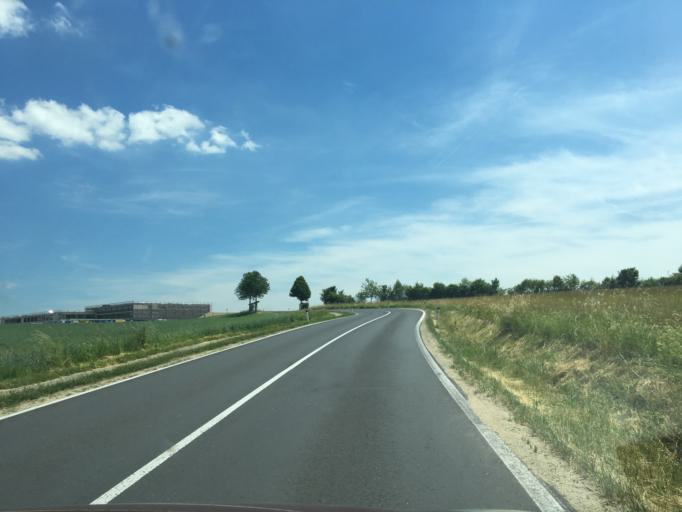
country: AT
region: Upper Austria
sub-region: Politischer Bezirk Urfahr-Umgebung
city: Engerwitzdorf
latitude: 48.3761
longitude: 14.5106
